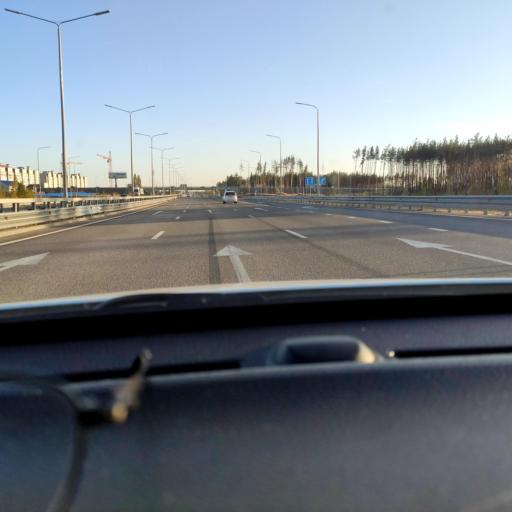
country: RU
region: Voronezj
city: Somovo
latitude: 51.7459
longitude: 39.3059
